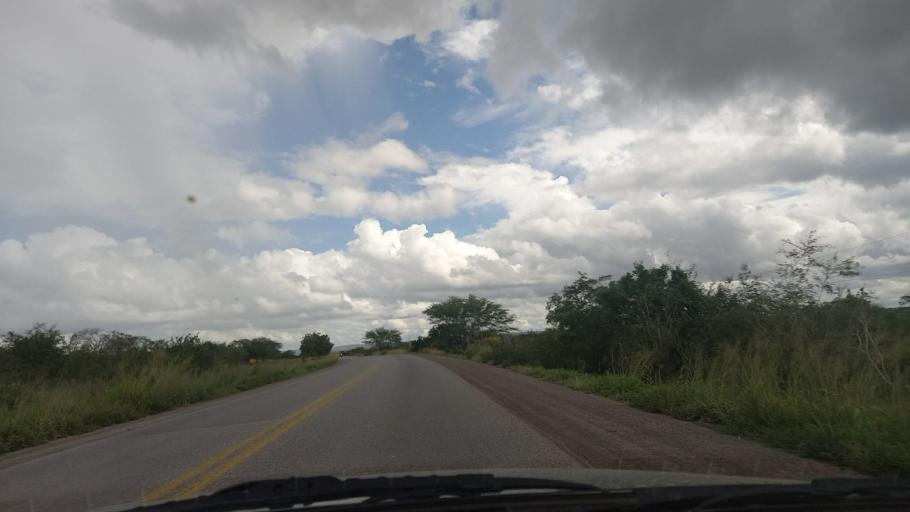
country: BR
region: Pernambuco
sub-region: Cachoeirinha
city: Cachoeirinha
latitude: -8.5365
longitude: -36.2668
